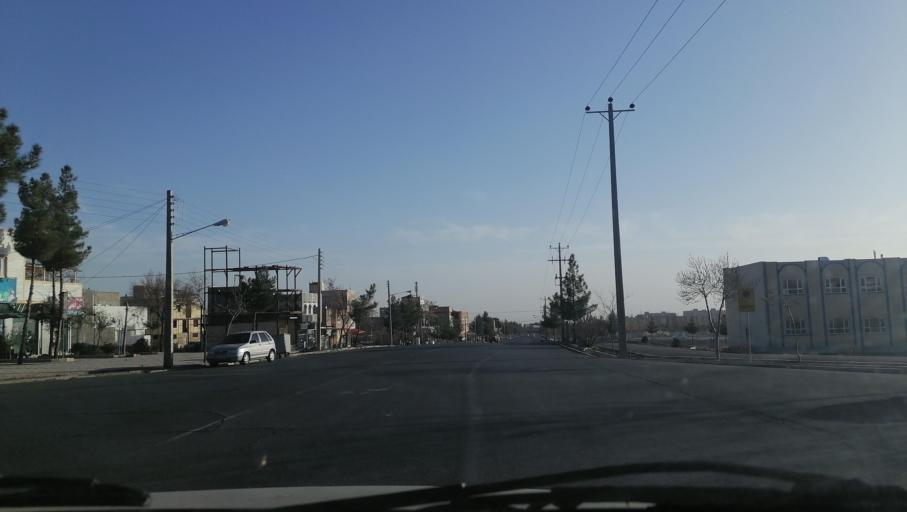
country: IR
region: Razavi Khorasan
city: Sabzevar
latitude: 36.2846
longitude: 57.6748
